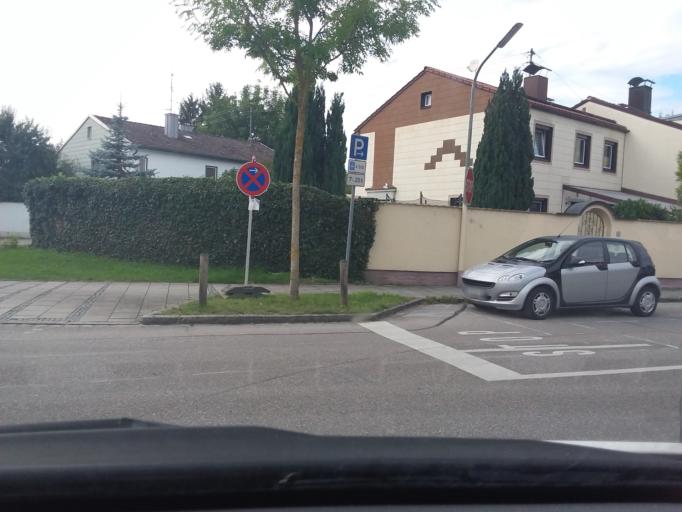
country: DE
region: Bavaria
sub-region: Upper Bavaria
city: Ismaning
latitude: 48.2282
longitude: 11.6833
